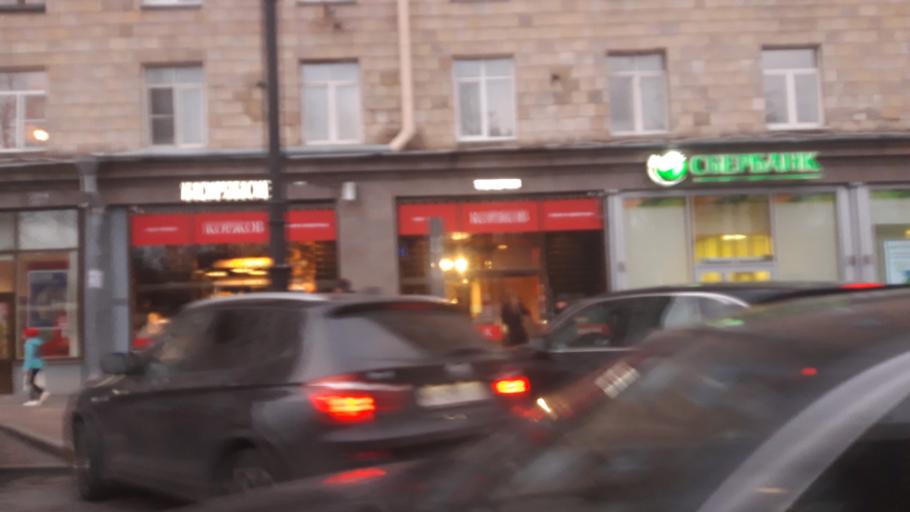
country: RU
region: St.-Petersburg
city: Kupchino
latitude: 59.8500
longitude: 30.3211
